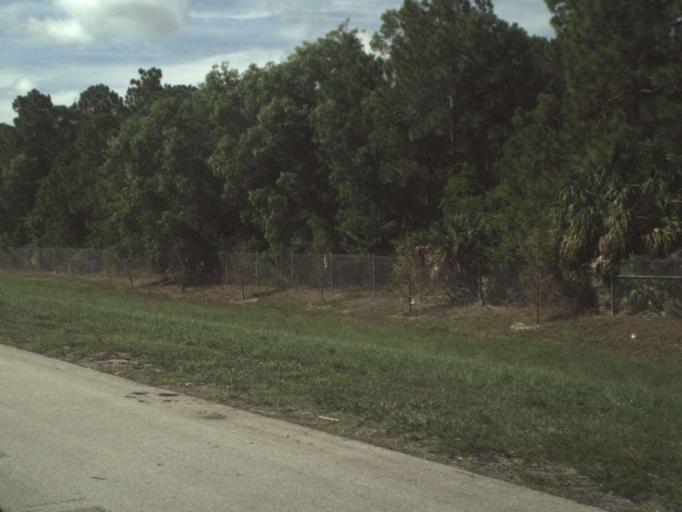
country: US
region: Florida
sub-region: Palm Beach County
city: Palm Beach Gardens
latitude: 26.8535
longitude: -80.1111
